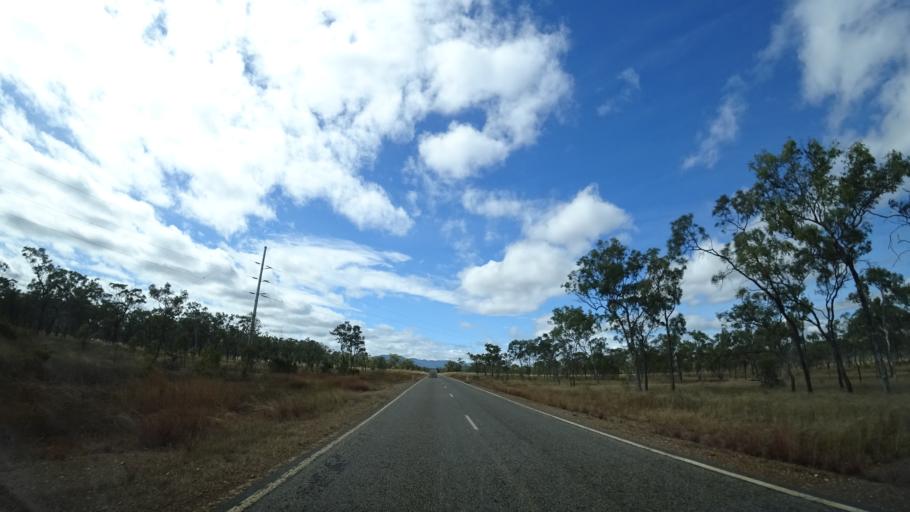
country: AU
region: Queensland
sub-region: Cairns
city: Port Douglas
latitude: -16.4971
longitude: 144.9876
